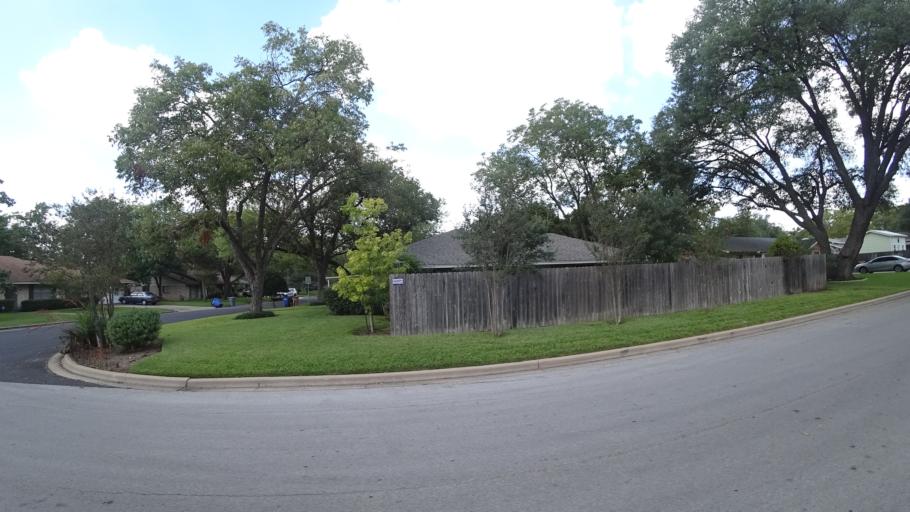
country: US
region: Texas
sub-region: Travis County
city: Austin
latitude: 30.3594
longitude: -97.7249
